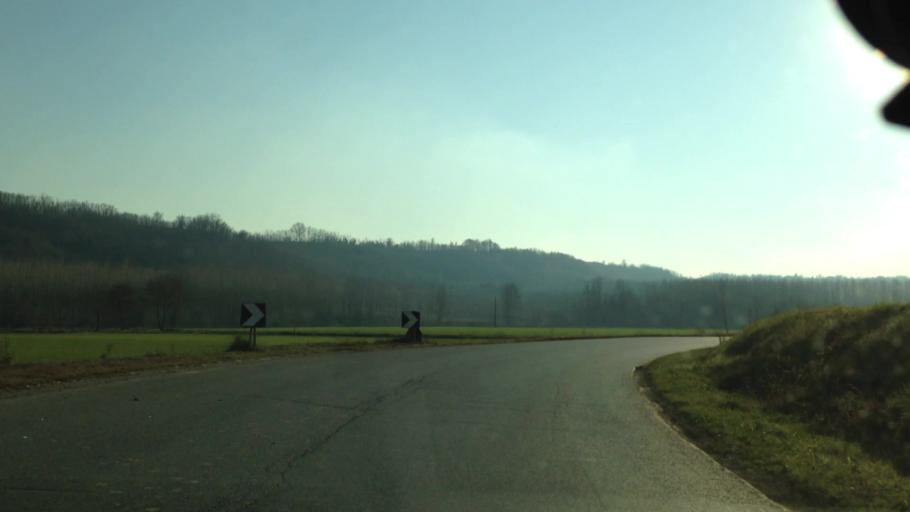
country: IT
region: Piedmont
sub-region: Provincia di Alessandria
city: Masio
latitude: 44.8474
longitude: 8.3979
